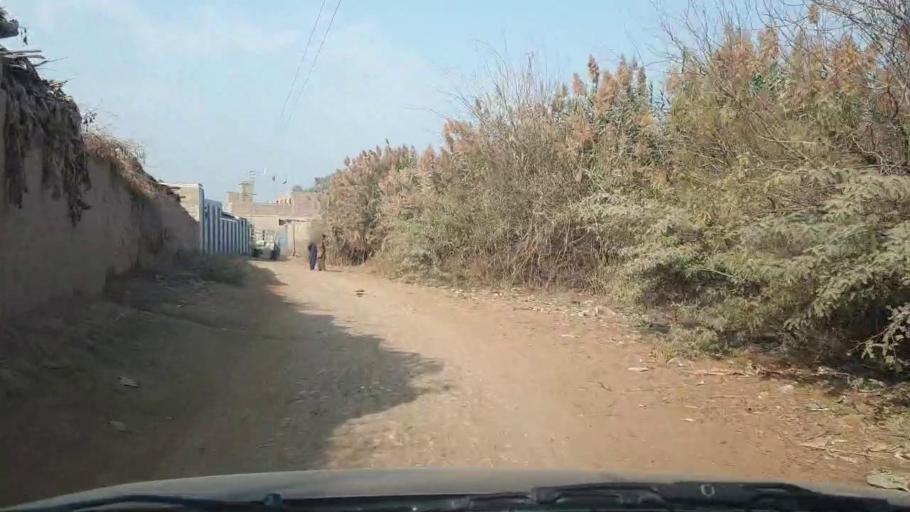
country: PK
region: Sindh
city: Hala
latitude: 25.8619
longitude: 68.4268
